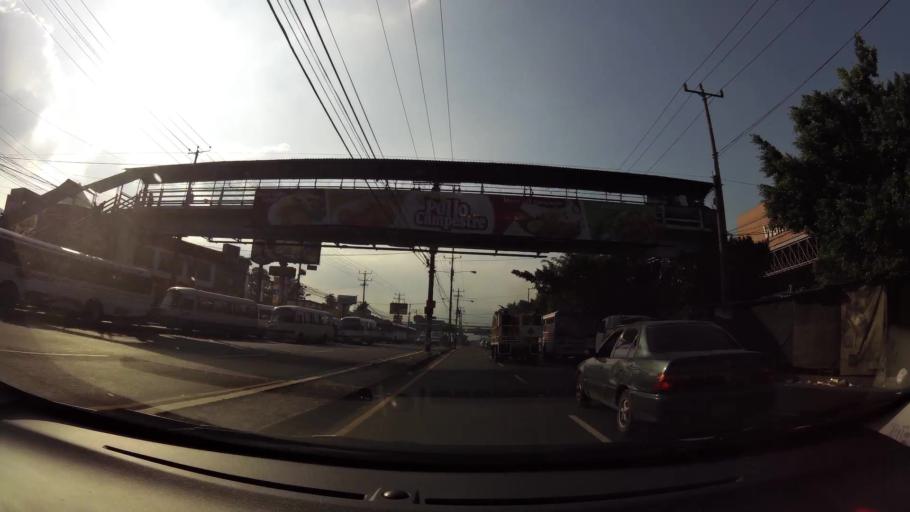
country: SV
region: San Salvador
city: Soyapango
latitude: 13.6998
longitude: -89.1506
